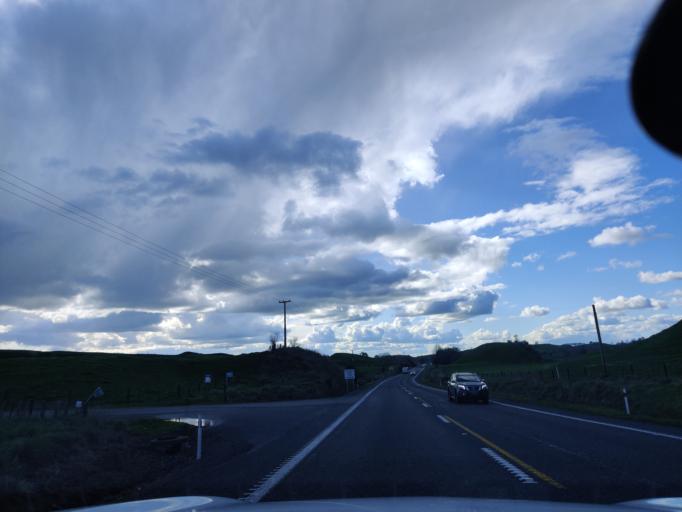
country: NZ
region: Waikato
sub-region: South Waikato District
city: Tokoroa
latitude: -38.1559
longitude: 175.8528
